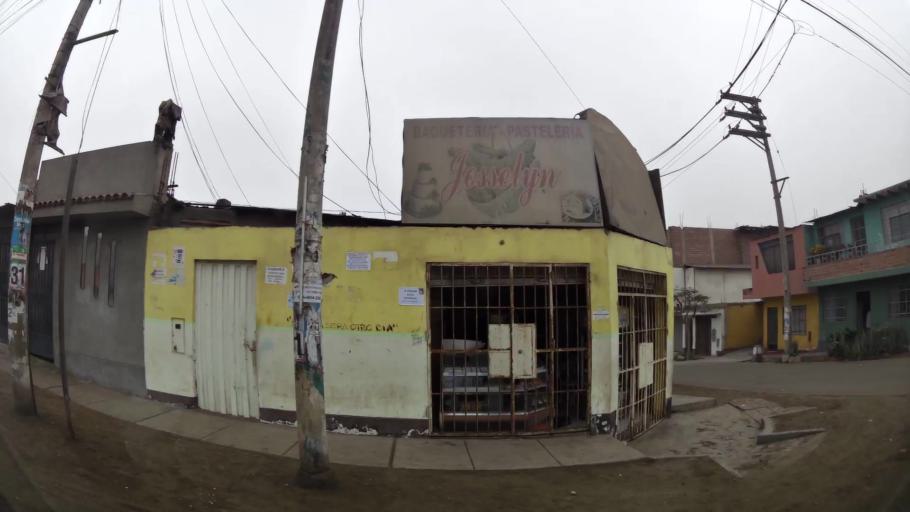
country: PE
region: Lima
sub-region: Lima
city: Santa Rosa
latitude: -11.8146
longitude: -77.1334
